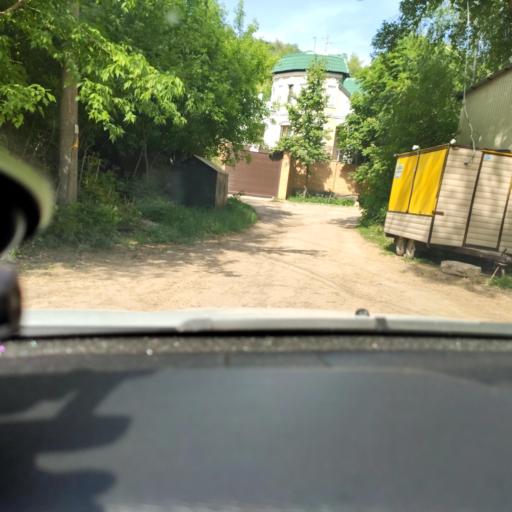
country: RU
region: Samara
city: Volzhskiy
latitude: 53.3360
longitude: 50.1961
